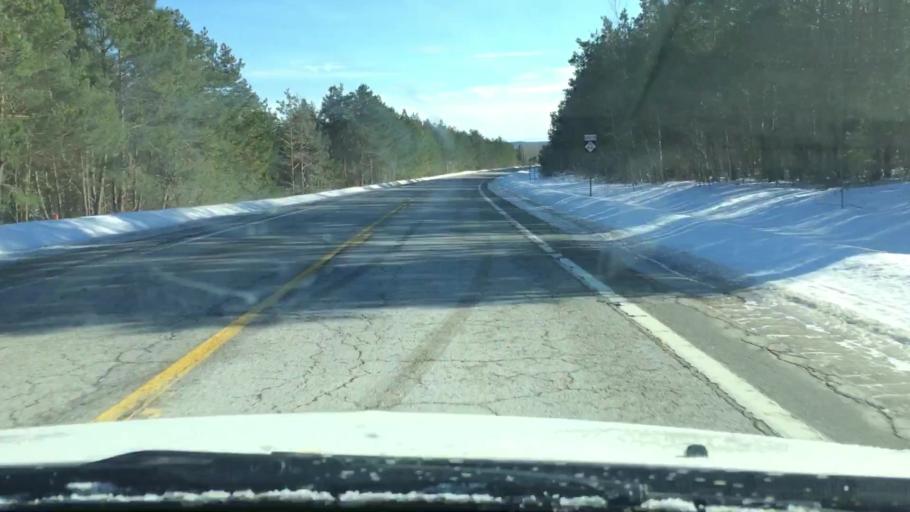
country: US
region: Michigan
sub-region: Charlevoix County
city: East Jordan
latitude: 45.0921
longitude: -85.0964
